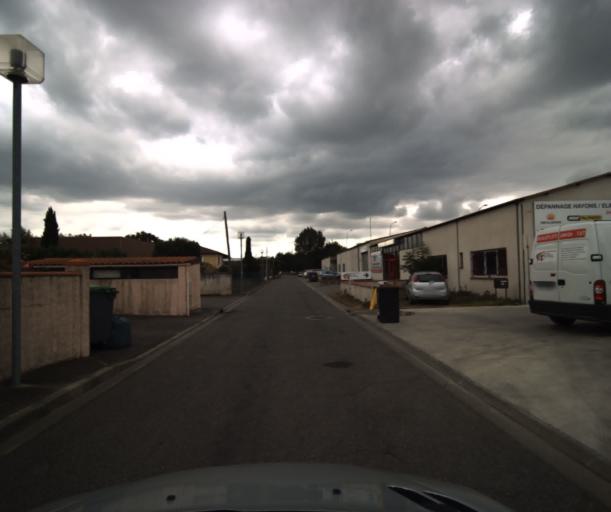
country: FR
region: Midi-Pyrenees
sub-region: Departement de la Haute-Garonne
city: Portet-sur-Garonne
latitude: 43.5376
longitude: 1.3946
